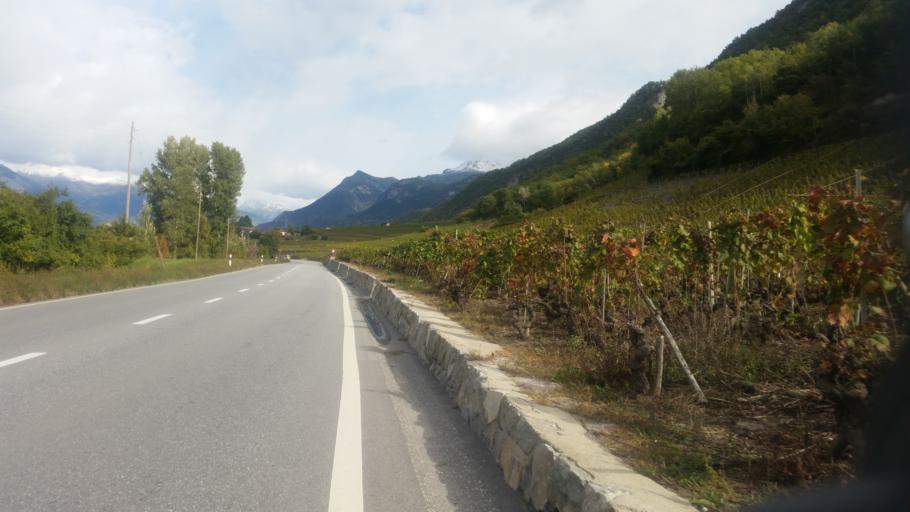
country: CH
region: Valais
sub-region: Sierre District
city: Grone
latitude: 46.2460
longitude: 7.4386
